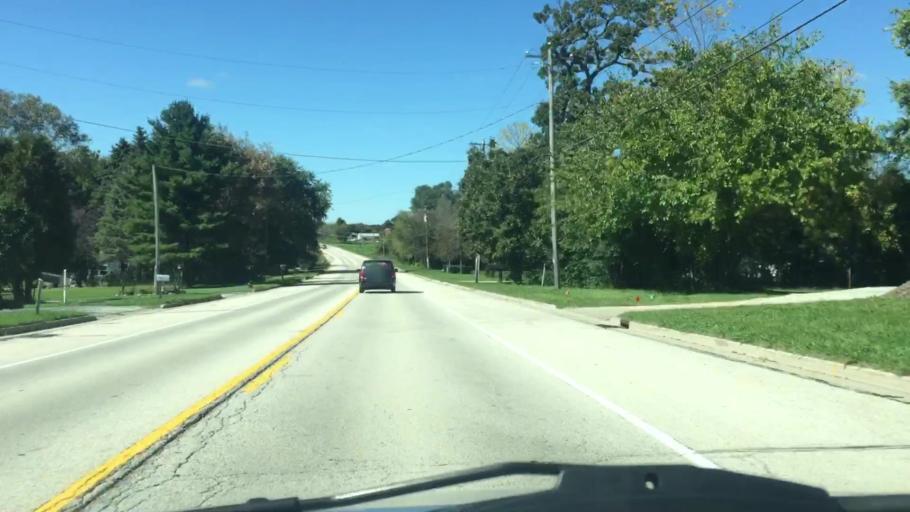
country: US
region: Wisconsin
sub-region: Waukesha County
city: Wales
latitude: 43.0204
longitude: -88.3525
